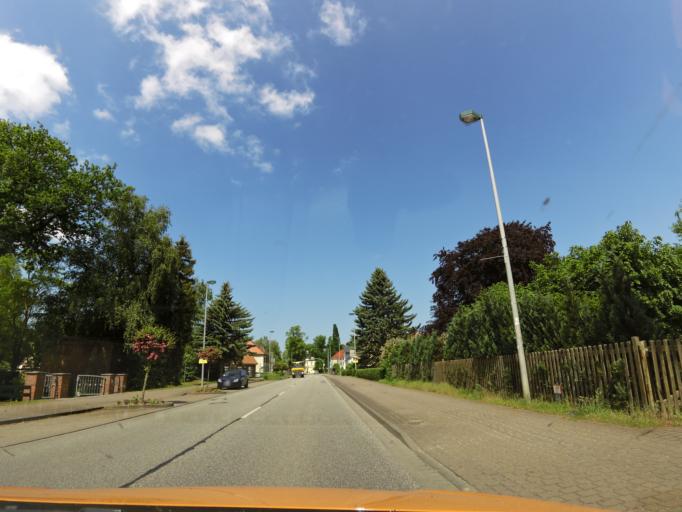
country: DE
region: Mecklenburg-Vorpommern
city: Rehna
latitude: 53.7781
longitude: 11.0501
